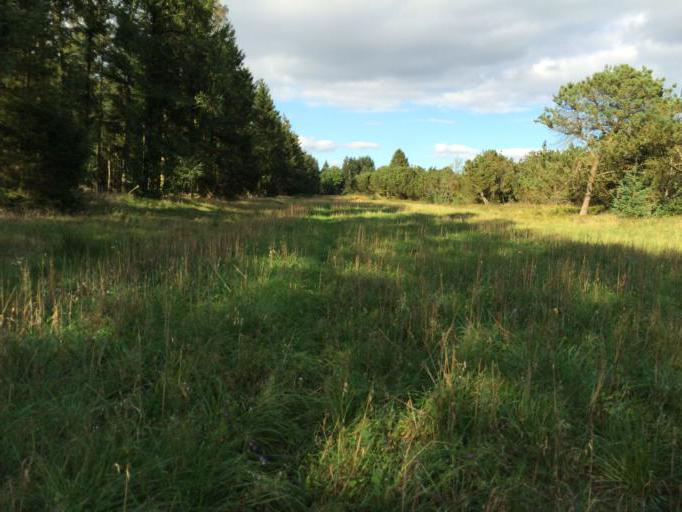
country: DK
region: Central Jutland
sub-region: Holstebro Kommune
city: Ulfborg
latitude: 56.2541
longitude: 8.4316
